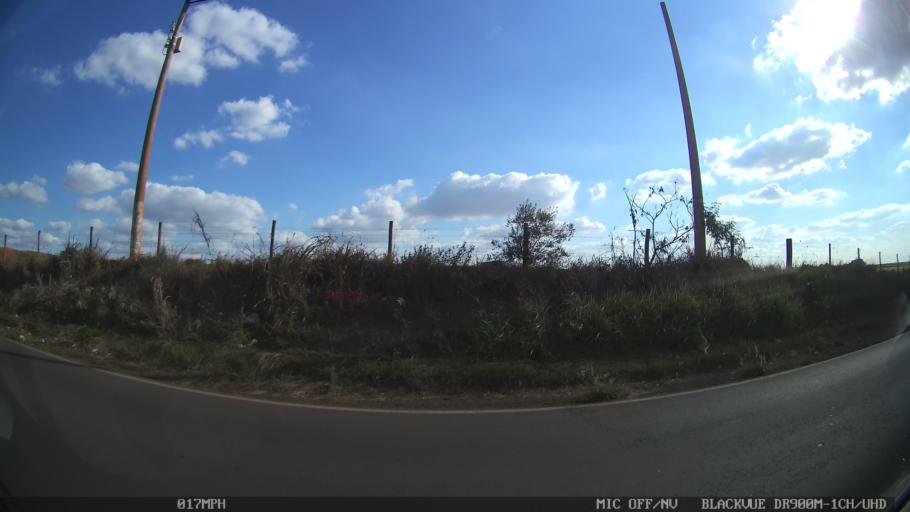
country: BR
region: Sao Paulo
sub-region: Nova Odessa
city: Nova Odessa
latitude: -22.8041
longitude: -47.3338
